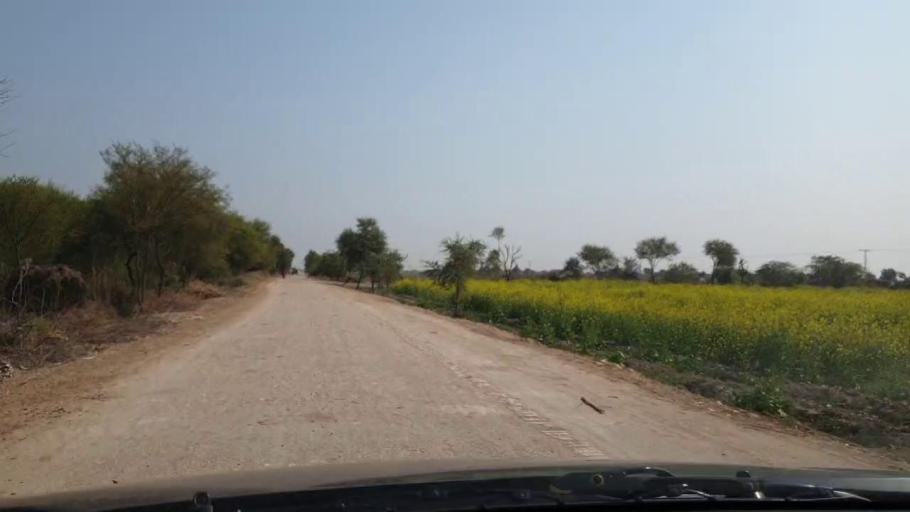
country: PK
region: Sindh
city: Jhol
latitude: 25.9976
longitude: 68.9153
